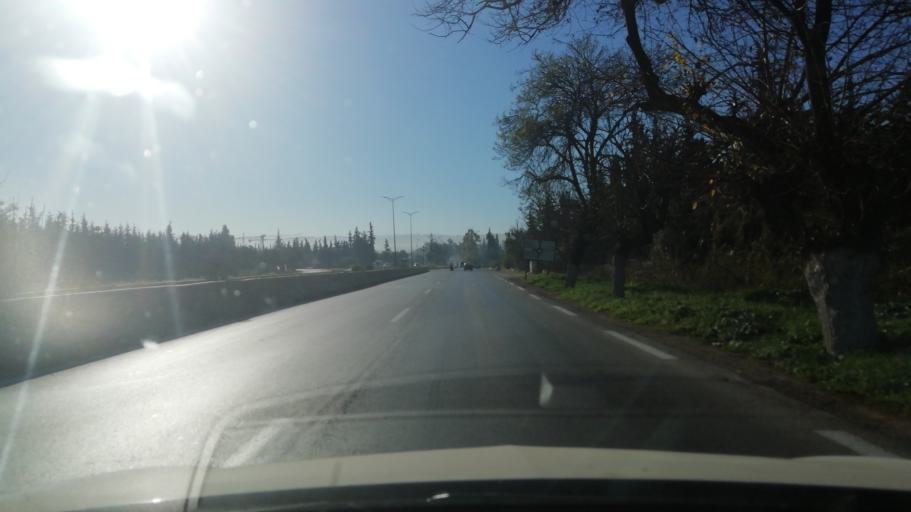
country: DZ
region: Tlemcen
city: Hennaya
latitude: 34.9656
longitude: -1.3776
